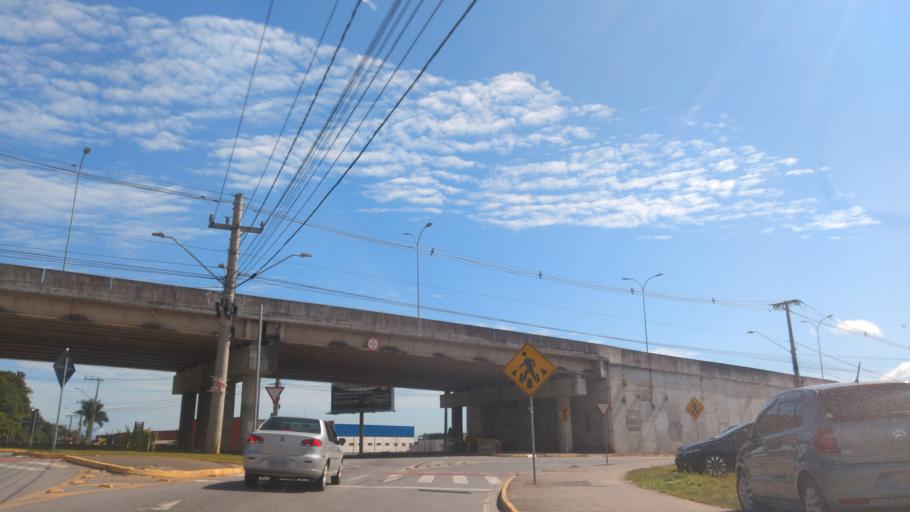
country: BR
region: Santa Catarina
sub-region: Joinville
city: Joinville
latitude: -26.2351
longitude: -48.8175
